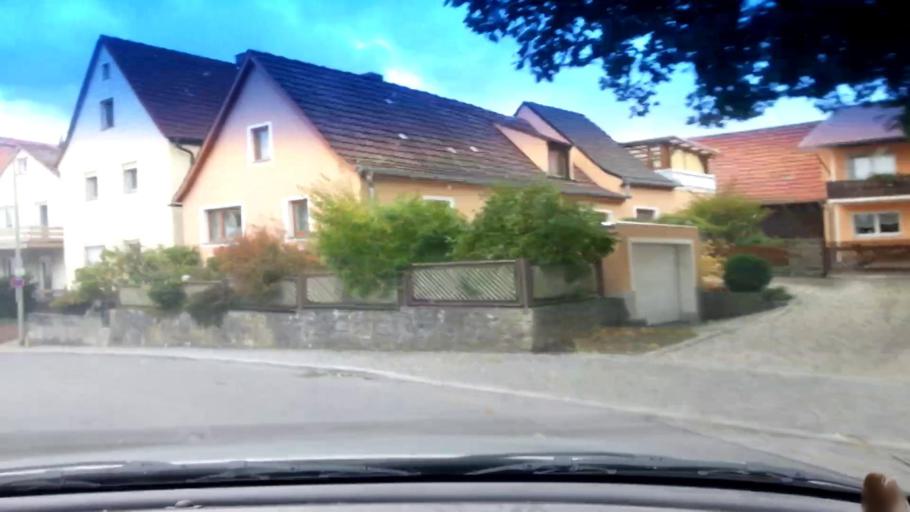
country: DE
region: Bavaria
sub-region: Upper Franconia
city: Priesendorf
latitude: 49.8954
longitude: 10.7267
